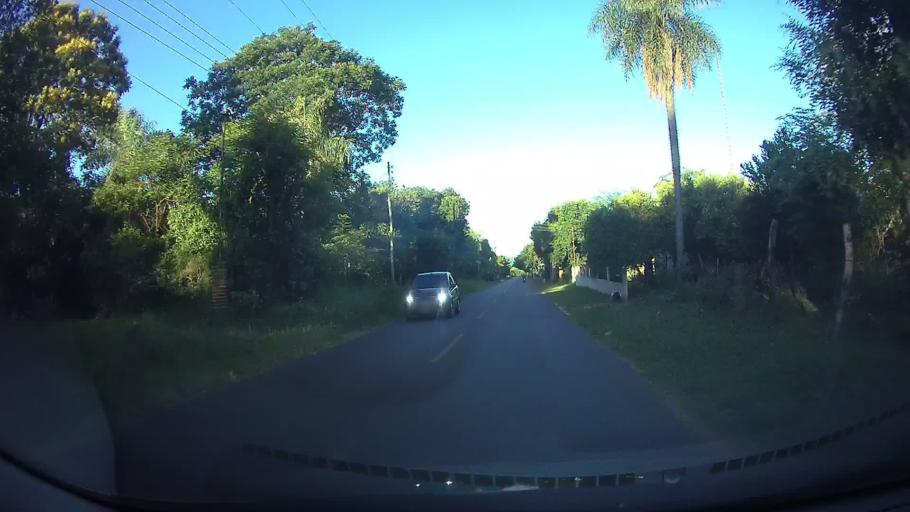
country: PY
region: Central
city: Aregua
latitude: -25.2843
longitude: -57.4007
